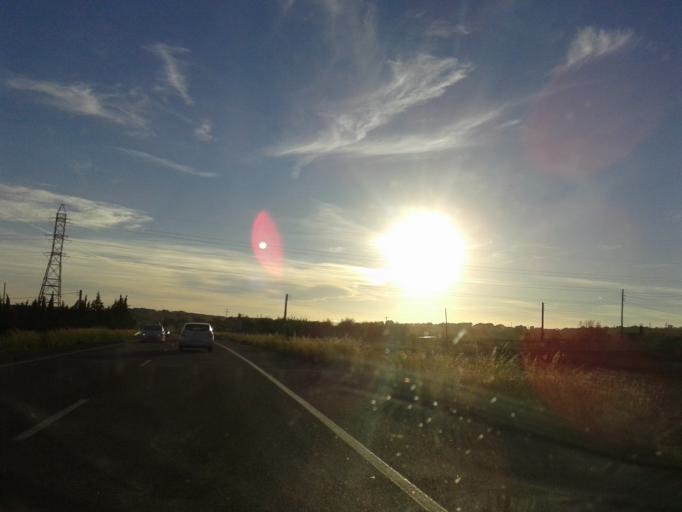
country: ES
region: Catalonia
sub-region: Provincia de Barcelona
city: Vilanova i la Geltru
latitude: 41.2331
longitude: 1.7118
